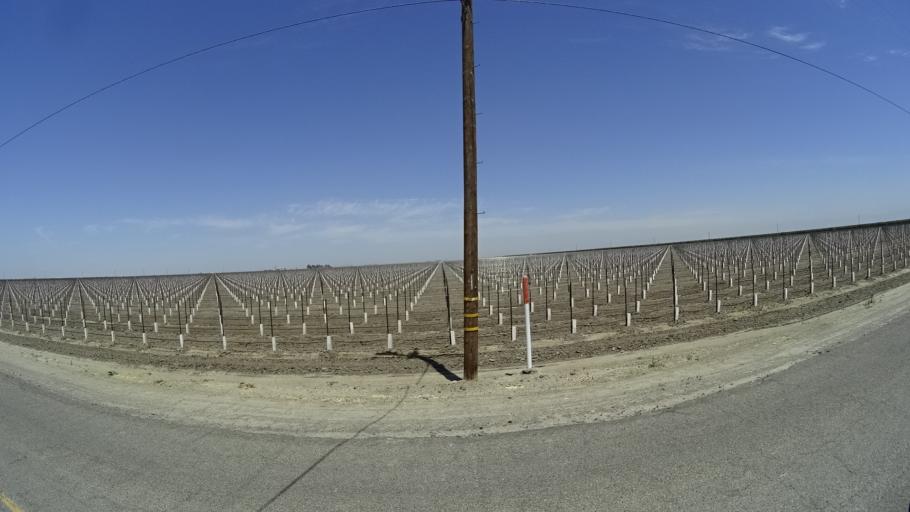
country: US
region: California
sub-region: Kings County
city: Corcoran
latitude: 36.1162
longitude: -119.6372
